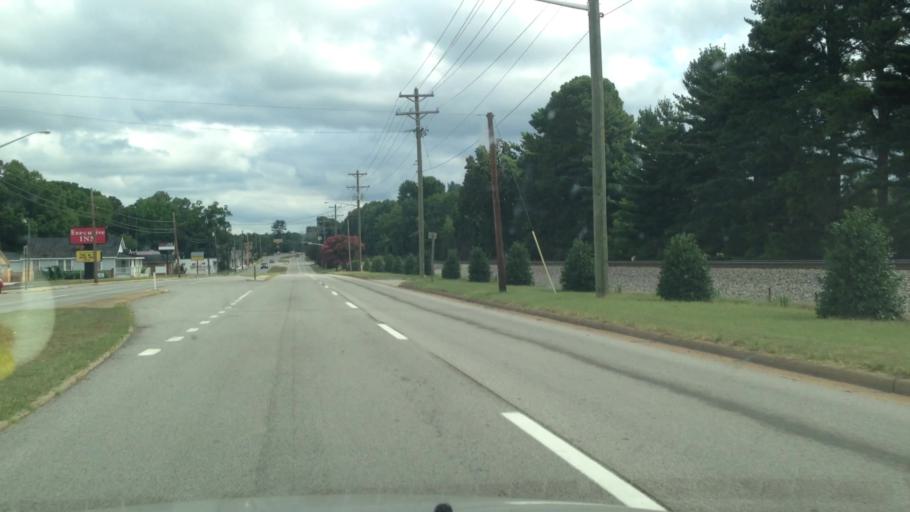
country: US
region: Virginia
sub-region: City of Danville
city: Danville
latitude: 36.5540
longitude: -79.4592
